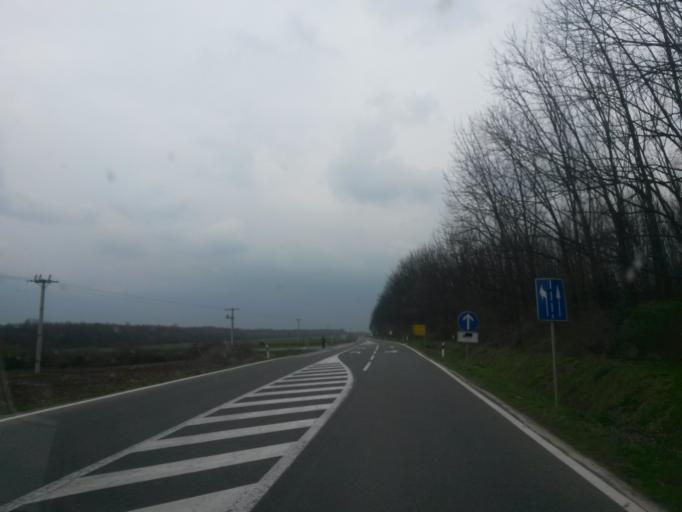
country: HR
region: Vukovarsko-Srijemska
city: Nijemci
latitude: 45.1974
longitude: 19.0233
